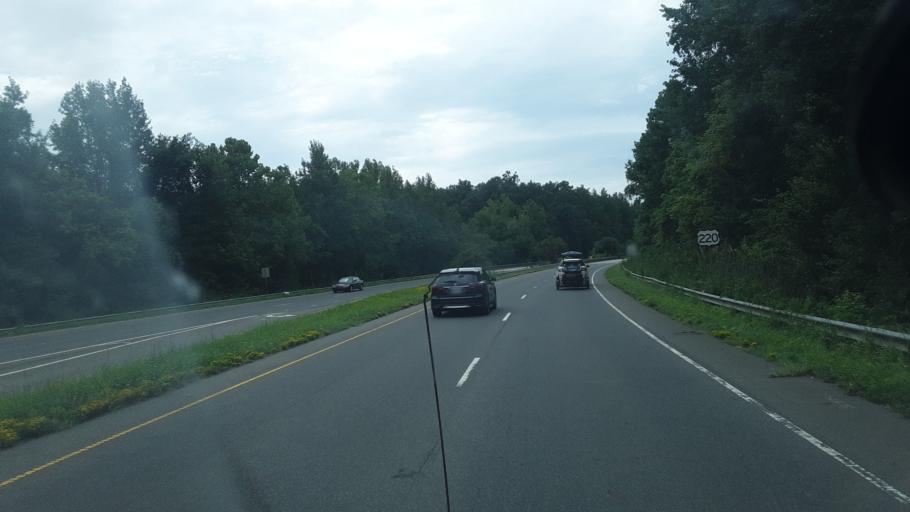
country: US
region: North Carolina
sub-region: Richmond County
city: Rockingham
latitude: 34.9475
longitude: -79.7757
